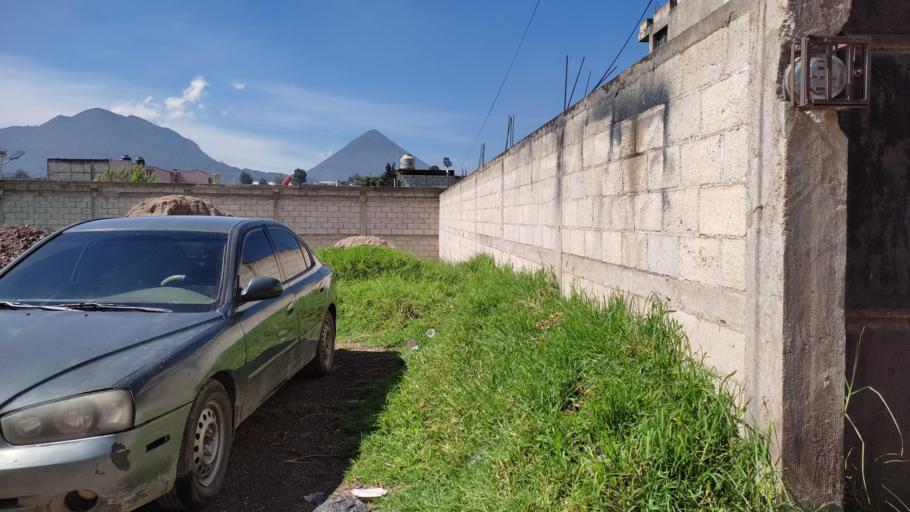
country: GT
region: Quetzaltenango
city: Quetzaltenango
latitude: 14.8541
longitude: -91.5231
